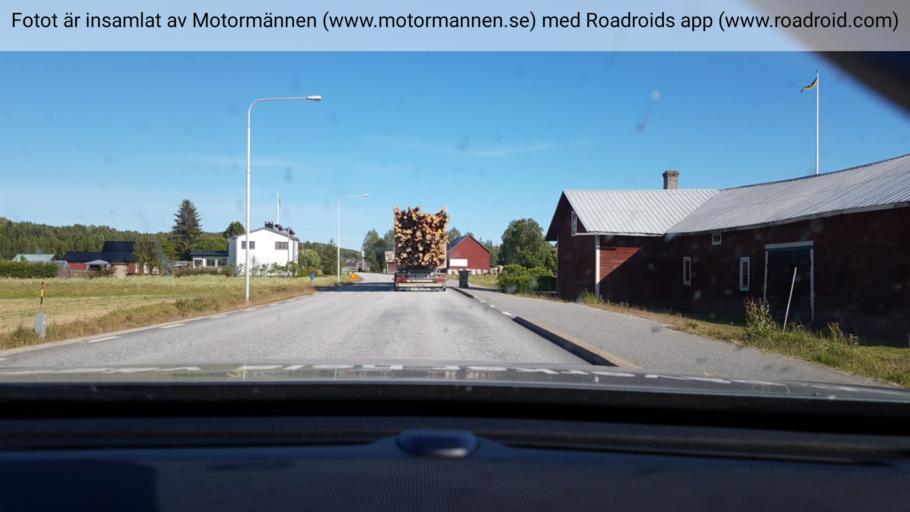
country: SE
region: Vaesterbotten
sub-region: Bjurholms Kommun
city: Bjurholm
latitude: 64.2564
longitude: 19.2939
